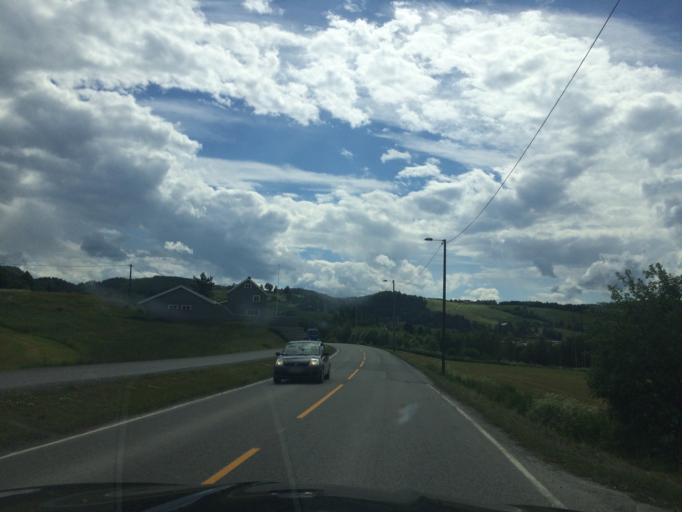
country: NO
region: Sor-Trondelag
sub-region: Selbu
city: Mebonden
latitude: 63.2477
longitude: 11.0918
